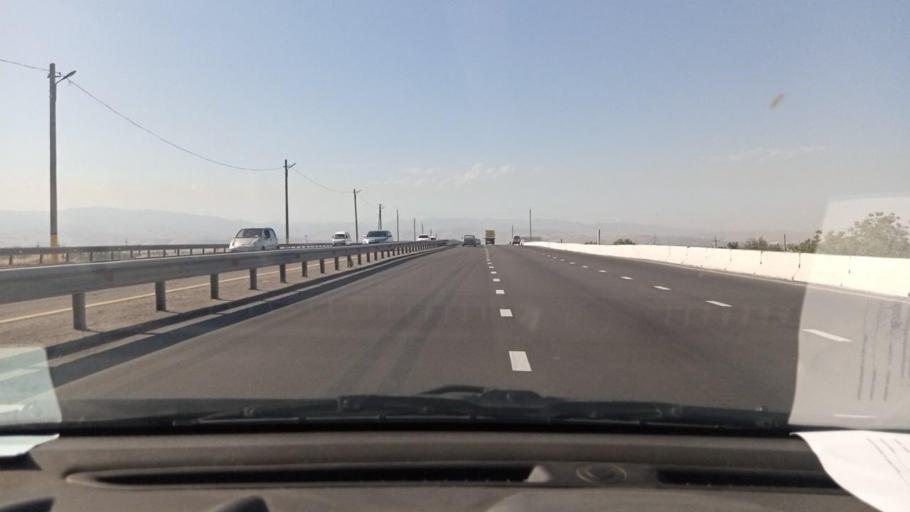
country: UZ
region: Toshkent
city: Ohangaron
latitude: 40.9261
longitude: 69.5966
